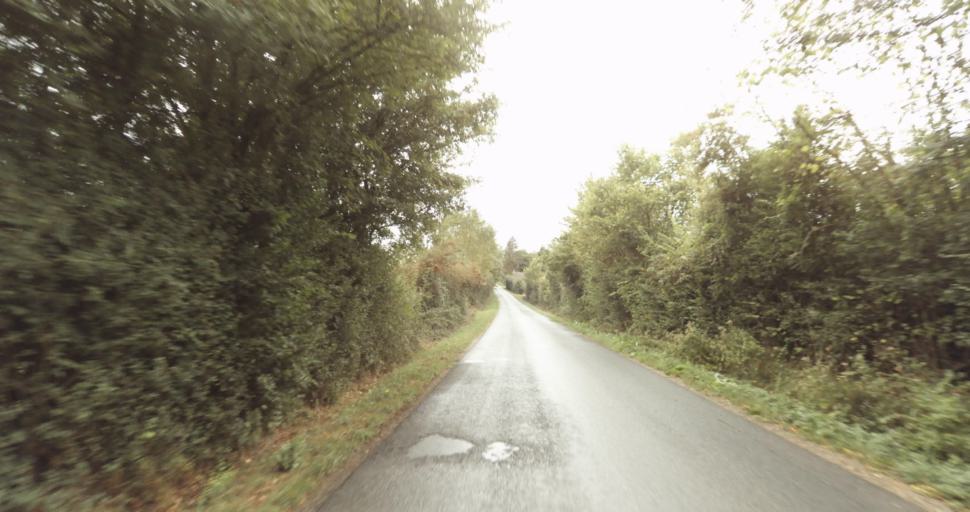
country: FR
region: Lower Normandy
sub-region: Departement de l'Orne
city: Vimoutiers
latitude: 48.8901
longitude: 0.2121
